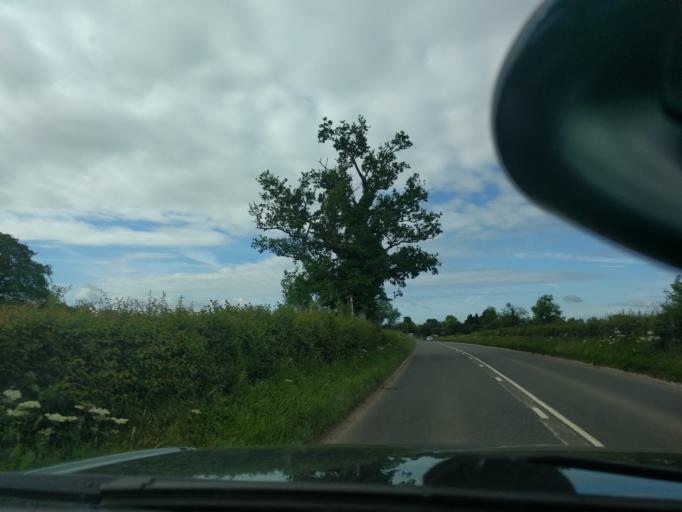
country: GB
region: England
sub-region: Wiltshire
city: Calne
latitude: 51.4585
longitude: -1.9908
